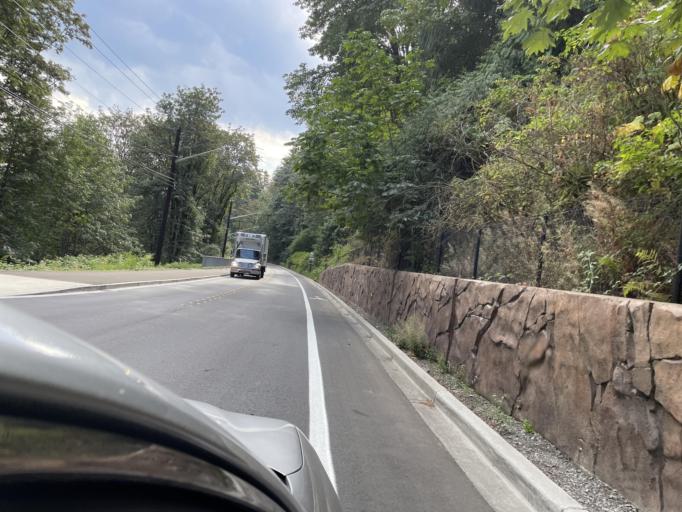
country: US
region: Washington
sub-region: King County
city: Eastgate
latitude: 47.5704
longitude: -122.1501
